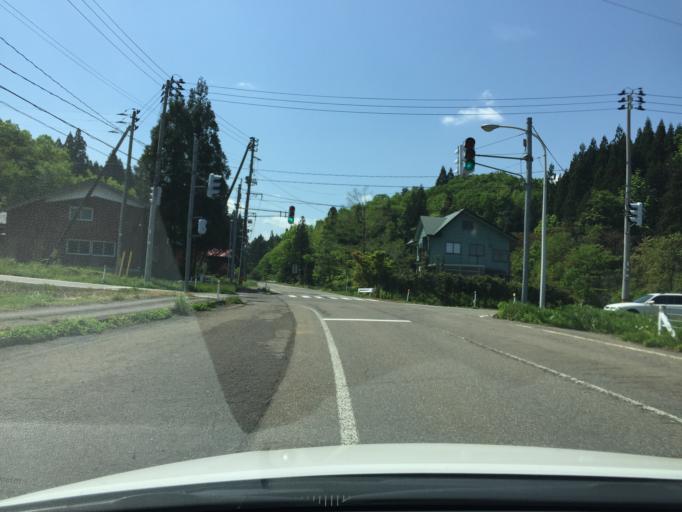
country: JP
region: Niigata
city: Tochio-honcho
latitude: 37.5393
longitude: 139.0918
